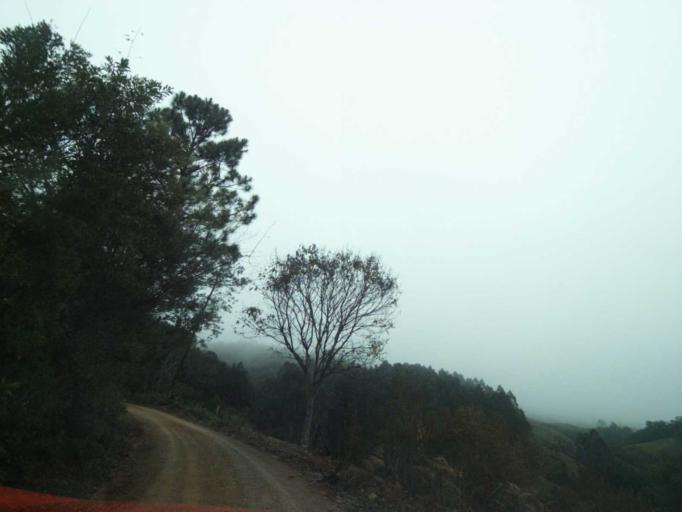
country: BR
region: Santa Catarina
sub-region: Anitapolis
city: Anitapolis
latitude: -27.9202
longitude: -49.1989
